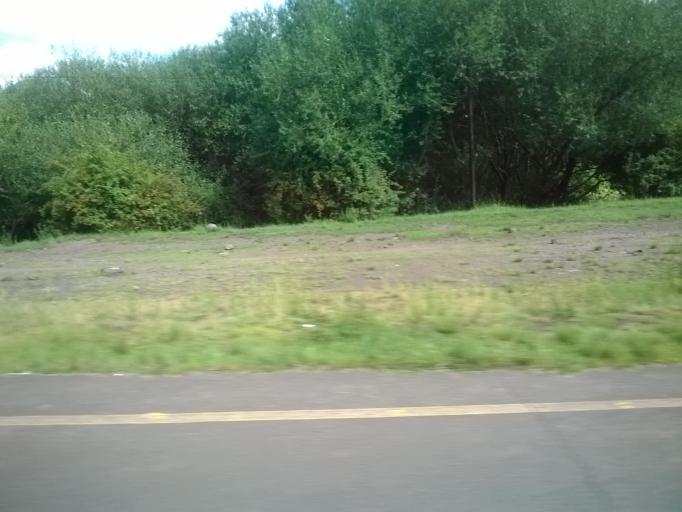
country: LS
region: Thaba-Tseka
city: Thaba-Tseka
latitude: -29.1421
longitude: 28.4863
